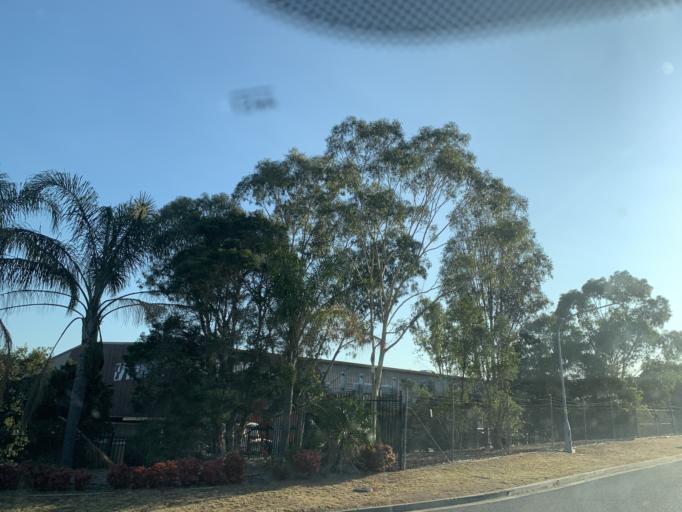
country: AU
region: New South Wales
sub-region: Blacktown
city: Doonside
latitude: -33.7940
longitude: 150.8730
